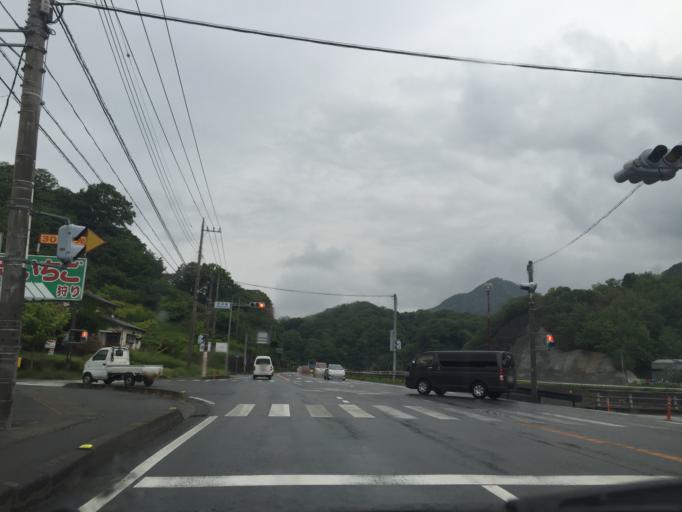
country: JP
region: Shizuoka
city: Mishima
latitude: 35.0473
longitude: 138.9143
